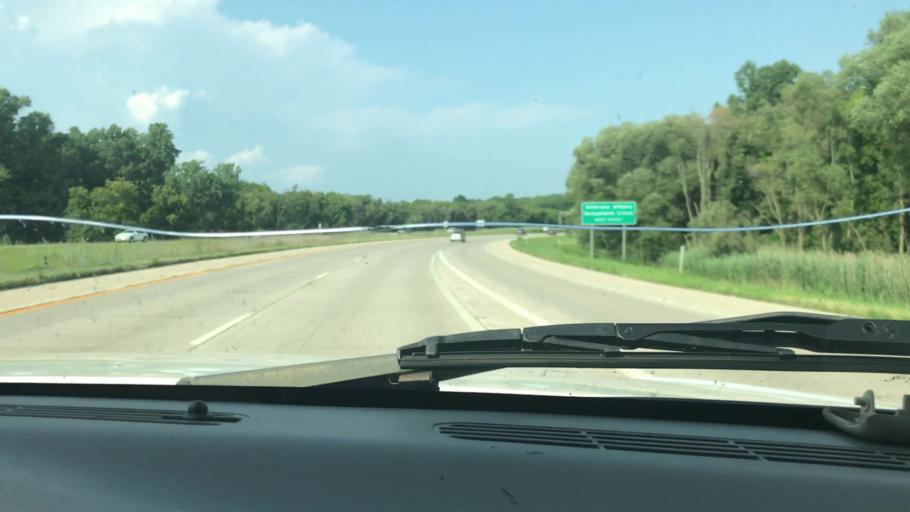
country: US
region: Wisconsin
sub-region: Brown County
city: Green Bay
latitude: 44.5228
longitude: -87.9488
